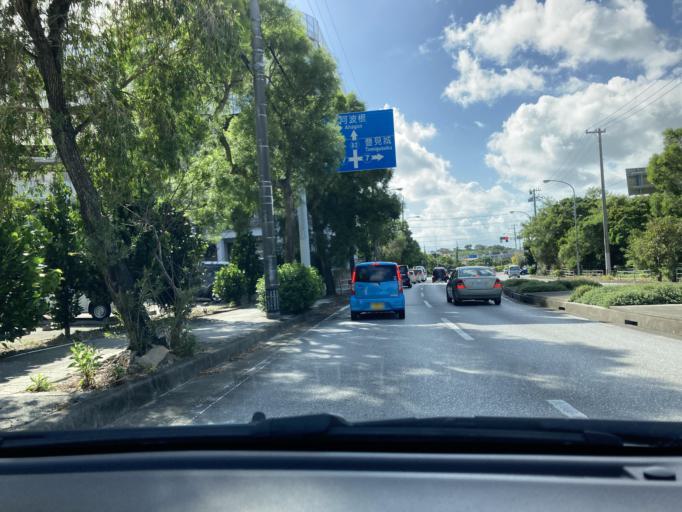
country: JP
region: Okinawa
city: Itoman
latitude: 26.1522
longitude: 127.6919
